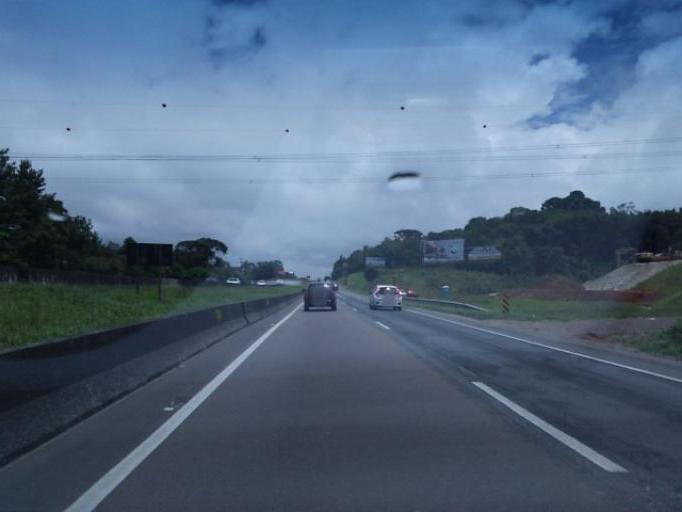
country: BR
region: Parana
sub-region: Sao Jose Dos Pinhais
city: Sao Jose dos Pinhais
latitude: -25.6317
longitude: -49.1629
